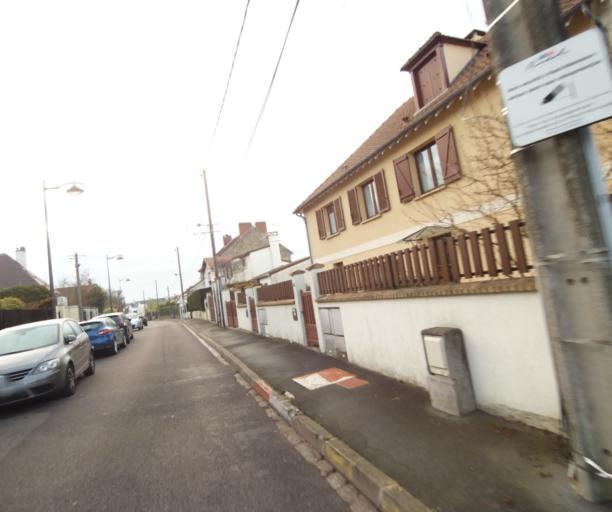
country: FR
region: Ile-de-France
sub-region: Departement des Hauts-de-Seine
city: Rueil-Malmaison
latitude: 48.8736
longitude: 2.2065
